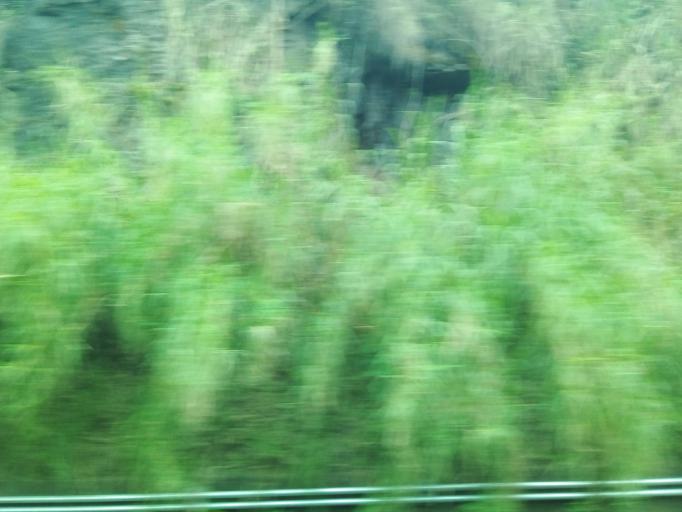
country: BR
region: Minas Gerais
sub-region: Nova Era
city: Nova Era
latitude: -19.7315
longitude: -43.0050
